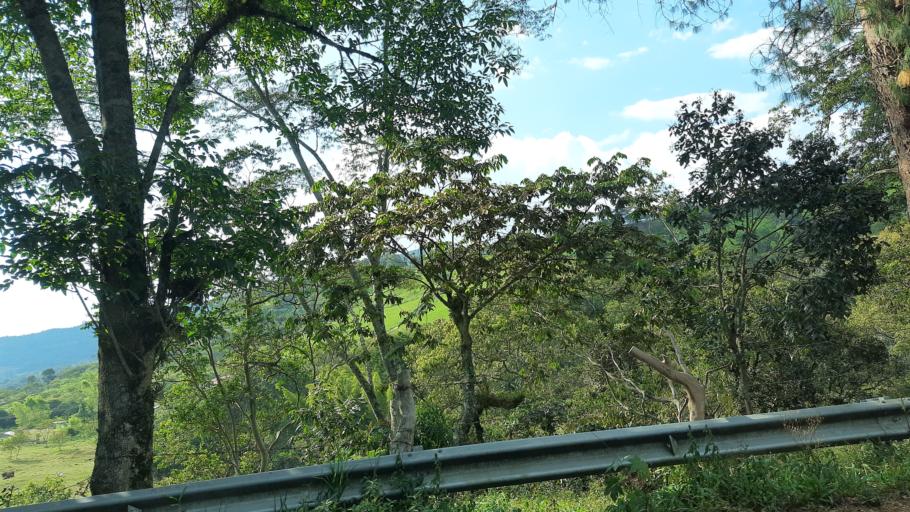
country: CO
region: Boyaca
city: Moniquira
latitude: 5.8402
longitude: -73.5887
